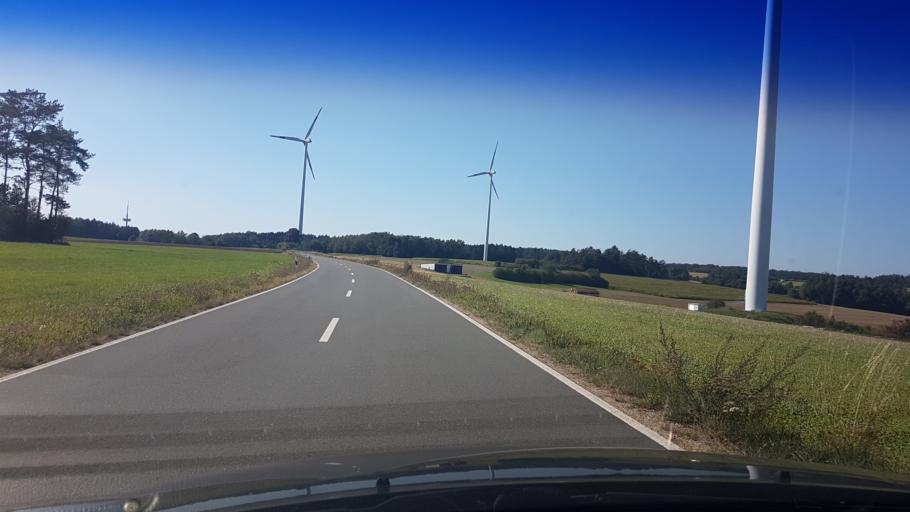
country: DE
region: Bavaria
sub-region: Upper Franconia
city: Heiligenstadt
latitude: 49.8553
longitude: 11.1023
